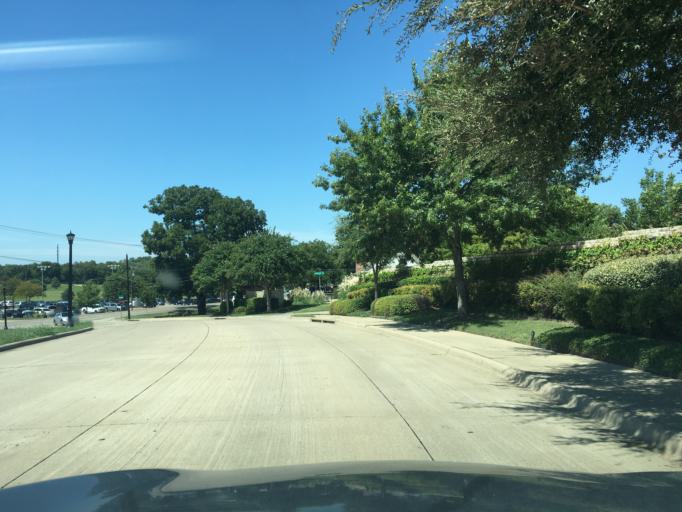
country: US
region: Texas
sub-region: Dallas County
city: Sachse
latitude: 32.9681
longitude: -96.6190
